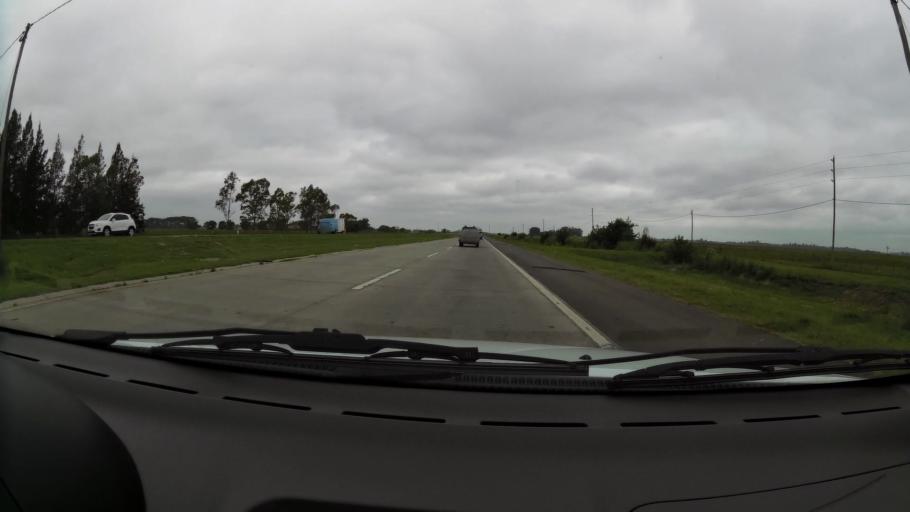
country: AR
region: Buenos Aires
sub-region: Partido de Brandsen
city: Brandsen
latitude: -35.0397
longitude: -58.1813
